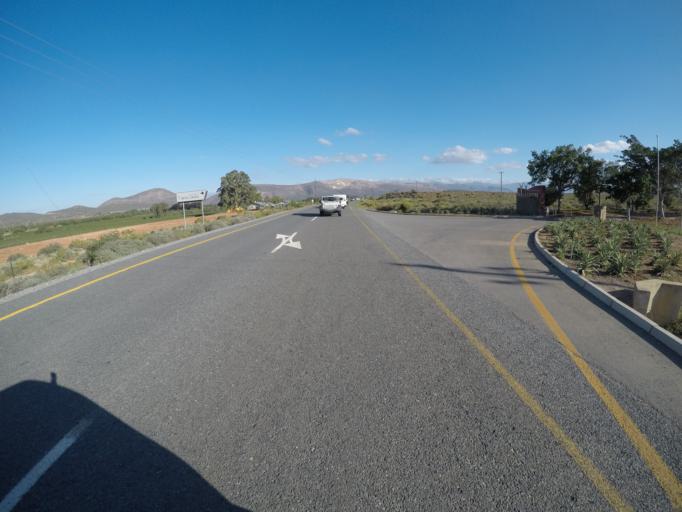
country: ZA
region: Western Cape
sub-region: Cape Winelands District Municipality
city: Ashton
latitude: -33.7933
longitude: 19.7802
